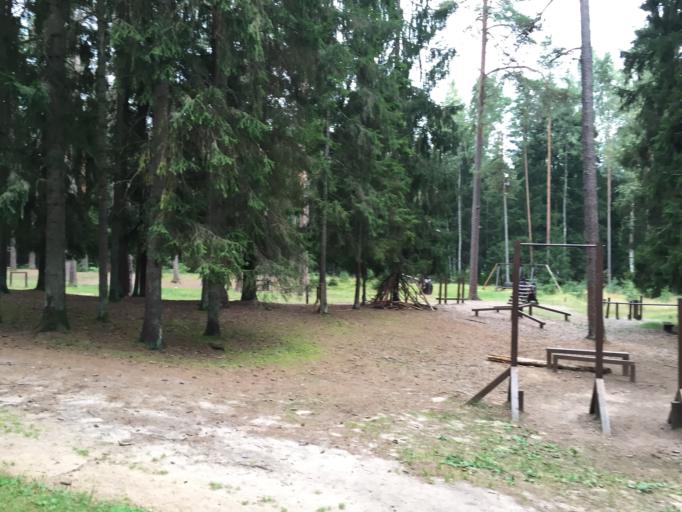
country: LV
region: Ogre
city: Ogre
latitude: 56.8295
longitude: 24.5863
